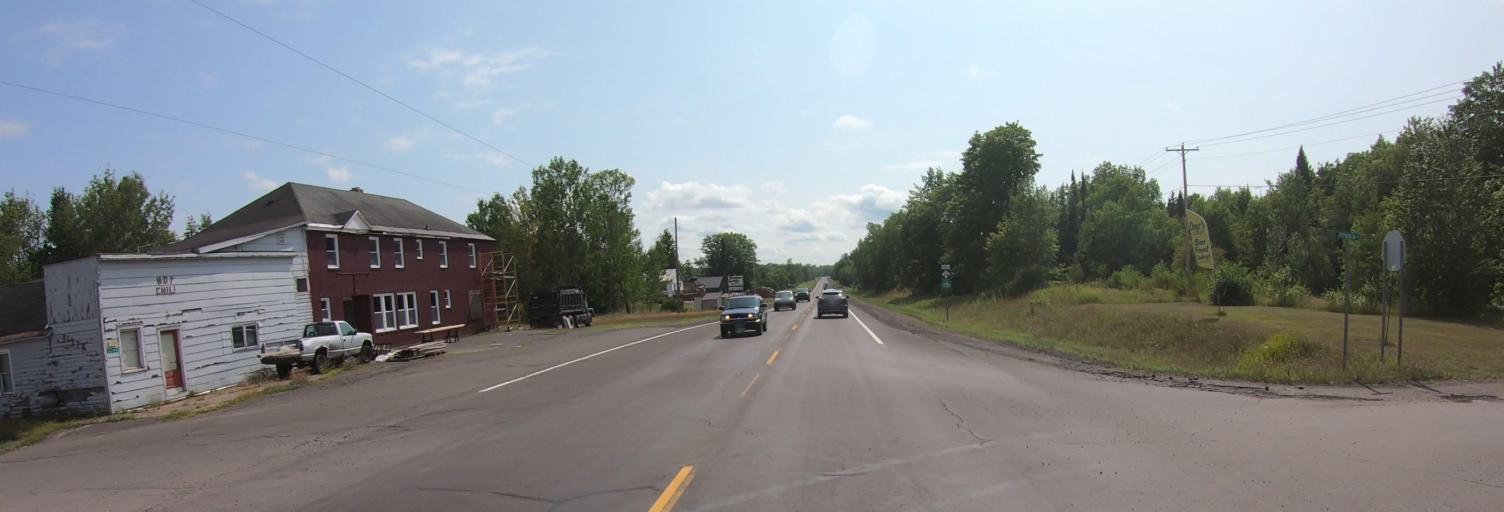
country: US
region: Michigan
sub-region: Houghton County
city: Hancock
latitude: 46.8848
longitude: -88.8636
